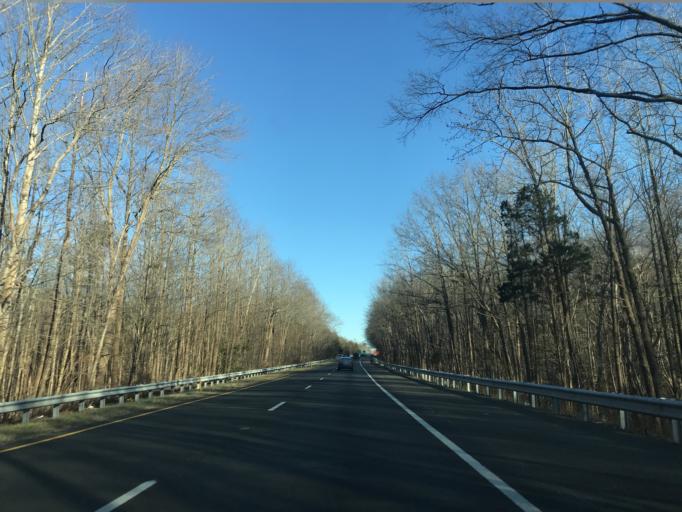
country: US
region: Maryland
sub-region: Prince George's County
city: Upper Marlboro
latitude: 38.8137
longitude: -76.7320
